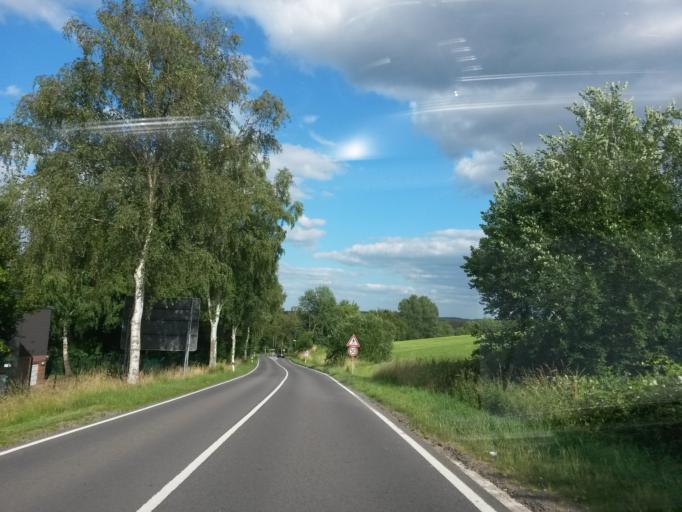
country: DE
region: North Rhine-Westphalia
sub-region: Regierungsbezirk Koln
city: Hennef
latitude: 50.8371
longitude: 7.3332
